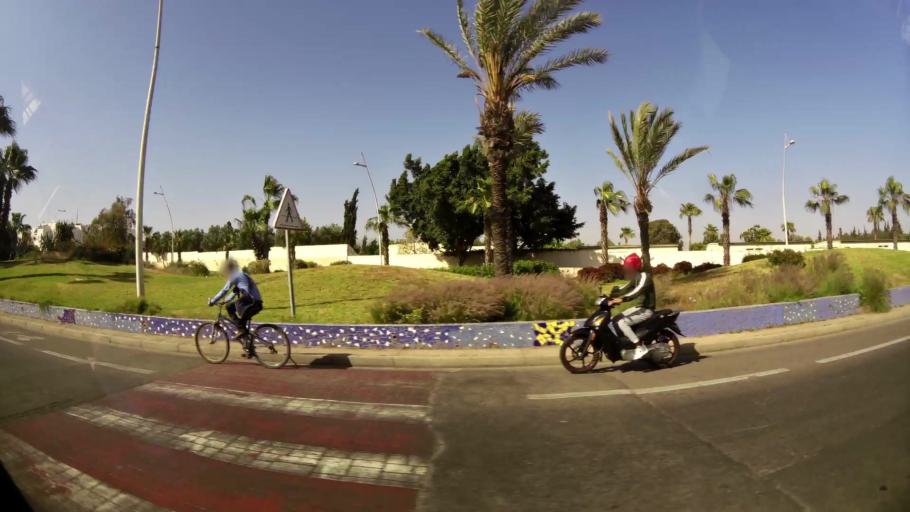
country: MA
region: Oued ed Dahab-Lagouira
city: Dakhla
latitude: 30.3820
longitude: -9.5666
